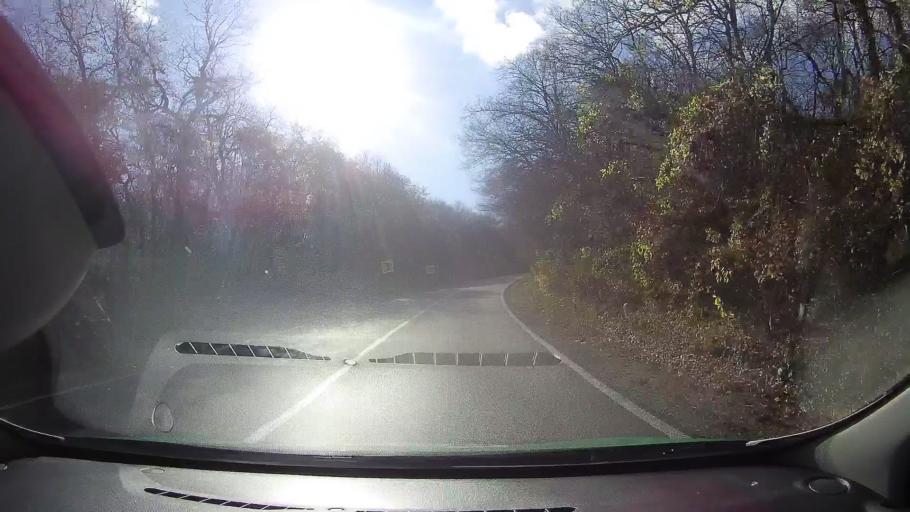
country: RO
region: Tulcea
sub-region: Oras Babadag
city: Babadag
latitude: 44.8426
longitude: 28.6976
